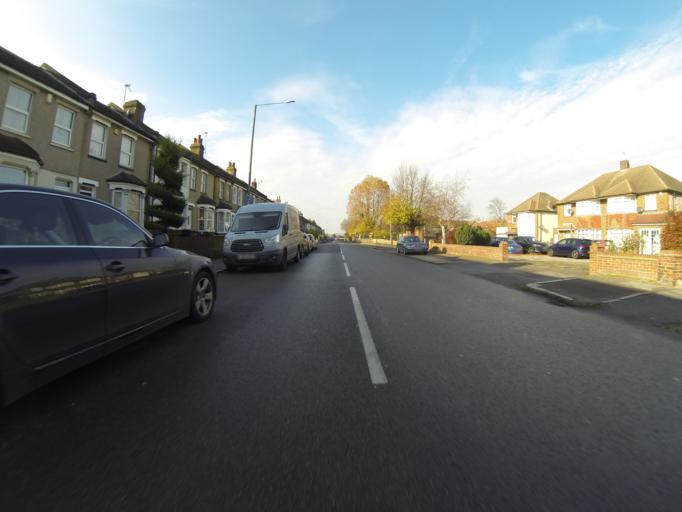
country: GB
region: England
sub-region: Kent
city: Dartford
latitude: 51.4465
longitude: 0.2047
